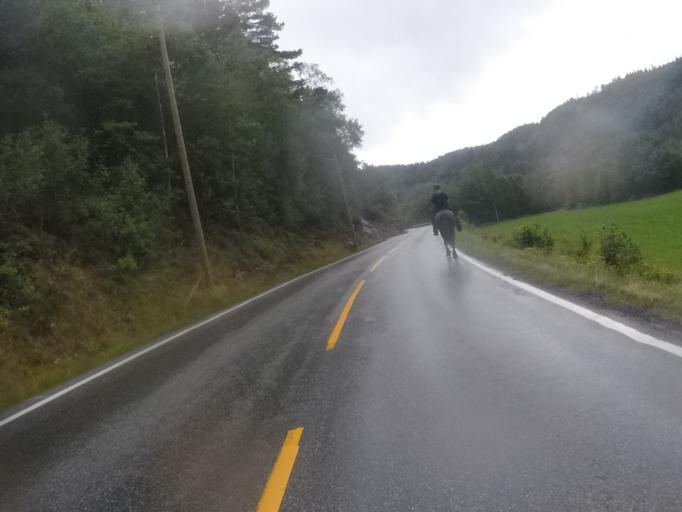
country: NO
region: Vest-Agder
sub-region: Songdalen
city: Nodeland
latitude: 58.1790
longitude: 7.8158
